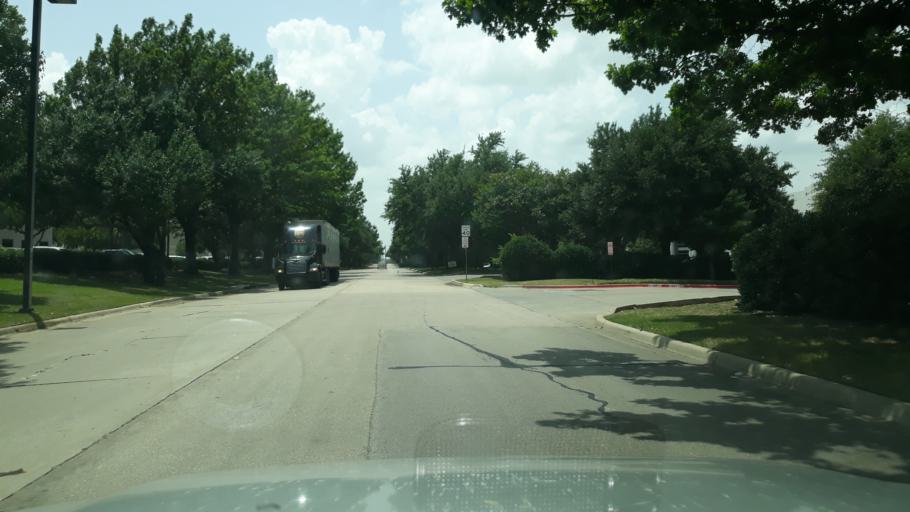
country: US
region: Texas
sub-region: Dallas County
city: Coppell
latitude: 32.9437
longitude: -97.0005
